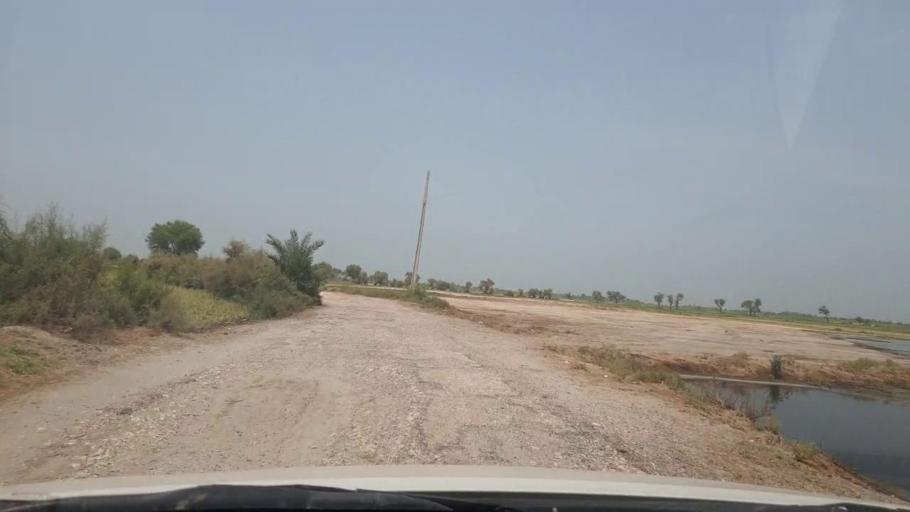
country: PK
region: Sindh
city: Rustam jo Goth
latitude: 28.0450
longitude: 68.7523
